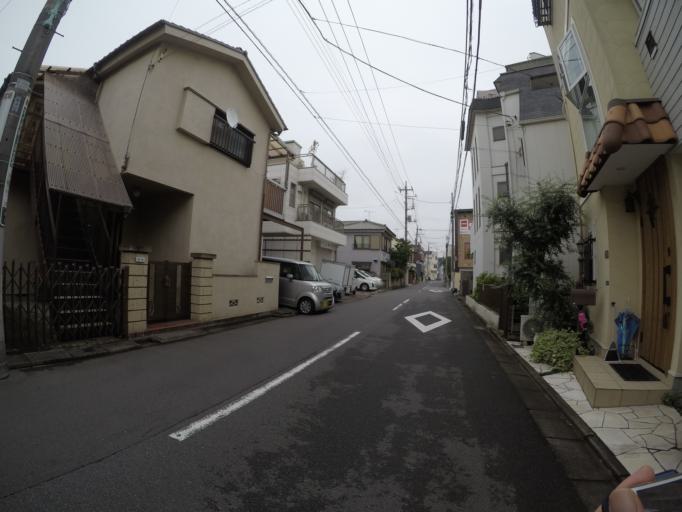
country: JP
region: Chiba
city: Matsudo
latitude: 35.7339
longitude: 139.8492
